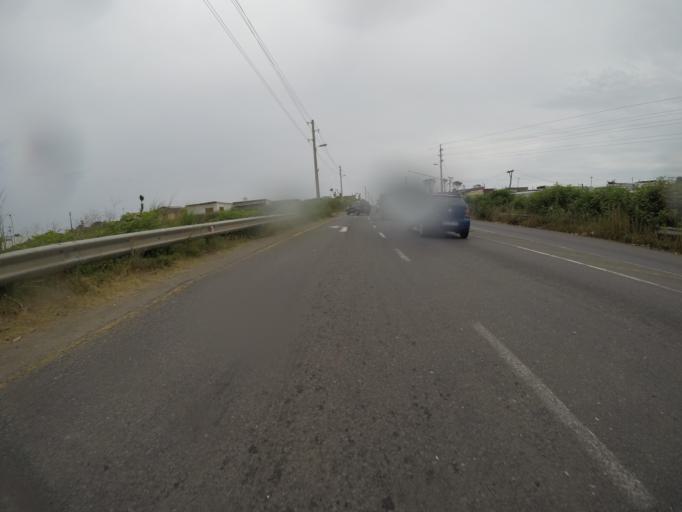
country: ZA
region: Eastern Cape
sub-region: Buffalo City Metropolitan Municipality
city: East London
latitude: -33.0009
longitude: 27.8417
